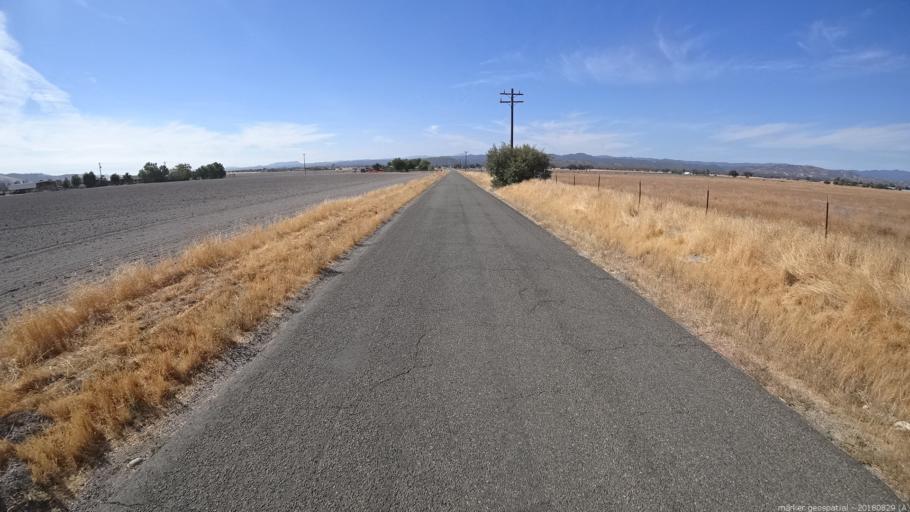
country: US
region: California
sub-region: Monterey County
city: King City
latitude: 35.9563
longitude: -121.0819
